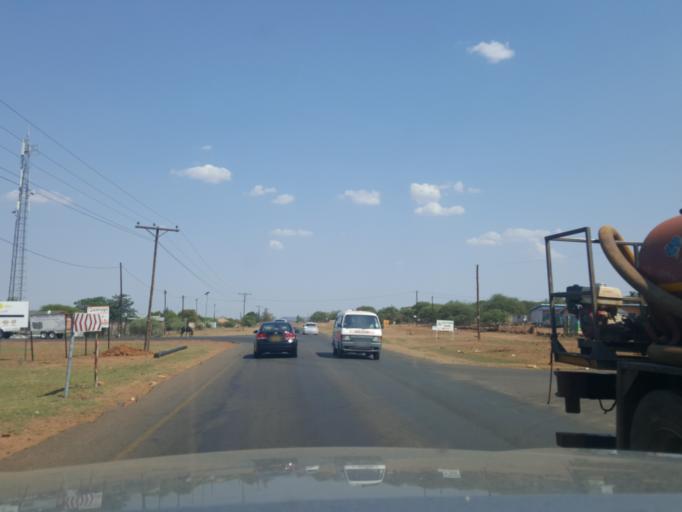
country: BW
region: South East
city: Ramotswa
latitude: -24.8404
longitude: 25.8226
